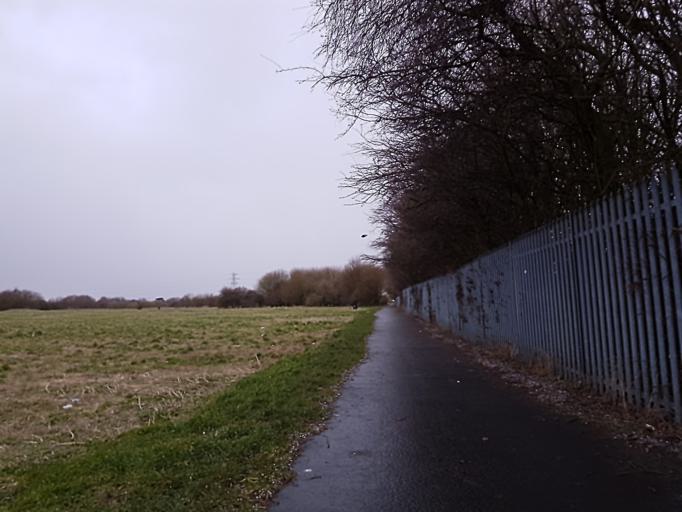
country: GB
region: England
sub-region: North East Lincolnshire
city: Grimbsy
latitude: 53.5647
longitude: -0.1182
